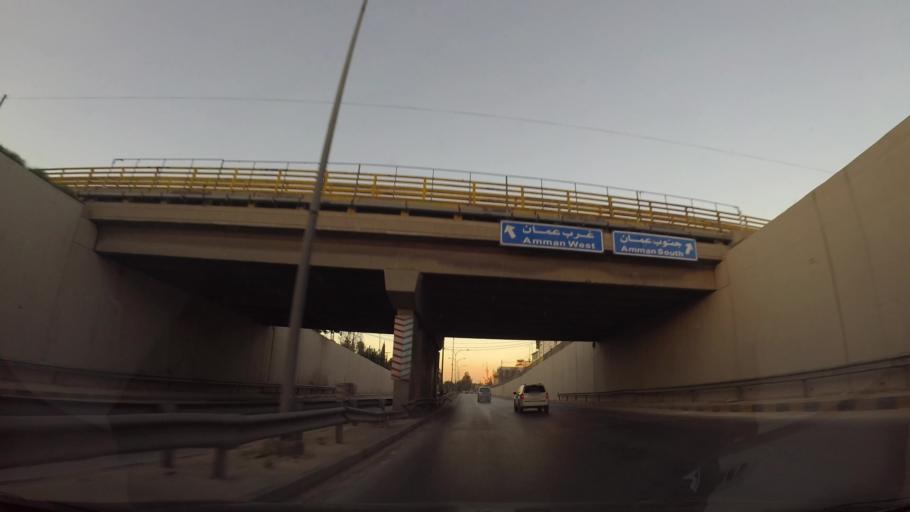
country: JO
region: Amman
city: Umm as Summaq
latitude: 31.8888
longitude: 35.8482
